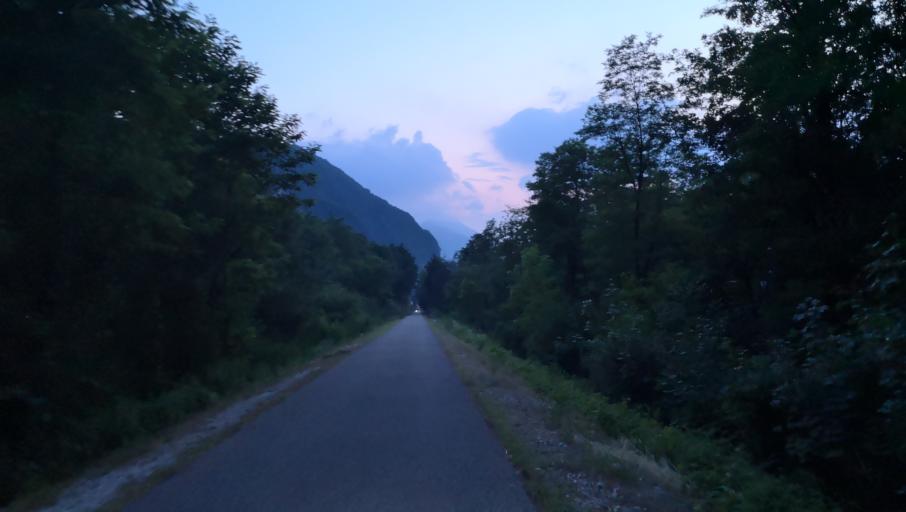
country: IT
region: Friuli Venezia Giulia
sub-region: Provincia di Udine
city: Resiutta
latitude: 46.3929
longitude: 13.2291
